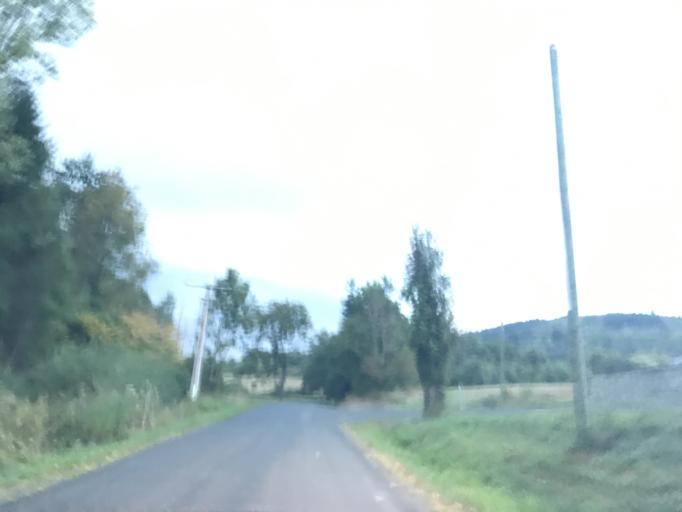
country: FR
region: Auvergne
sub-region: Departement du Puy-de-Dome
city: Escoutoux
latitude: 45.8186
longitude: 3.5596
